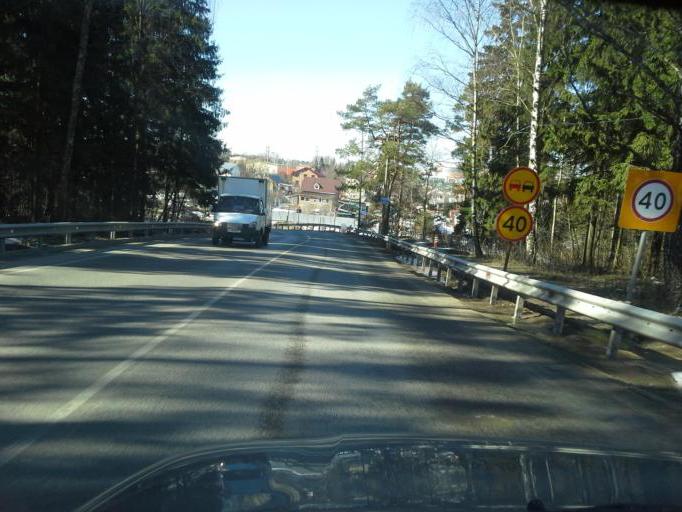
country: RU
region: Moskovskaya
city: Gorki Vtoryye
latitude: 55.6797
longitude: 37.1590
